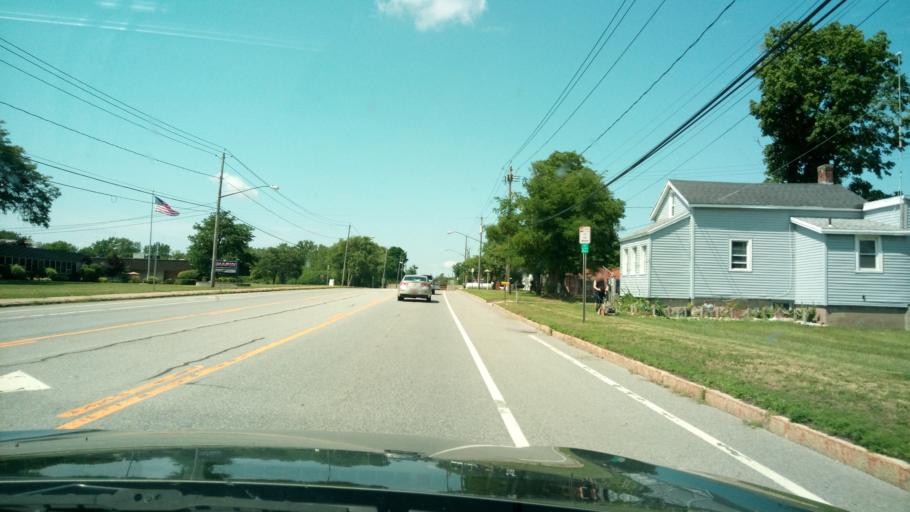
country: US
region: New York
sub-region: Genesee County
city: Batavia
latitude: 42.9829
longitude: -78.1653
